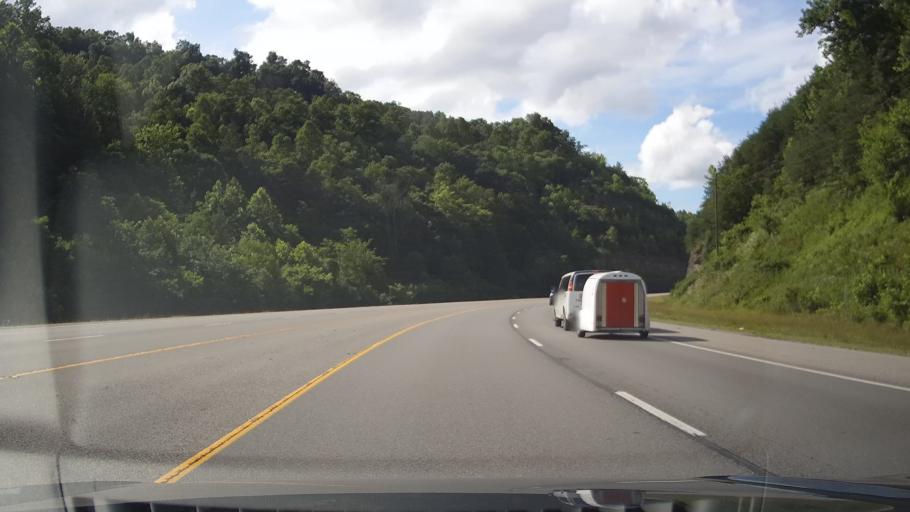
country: US
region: Kentucky
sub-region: Floyd County
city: Prestonsburg
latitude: 37.6664
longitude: -82.7920
